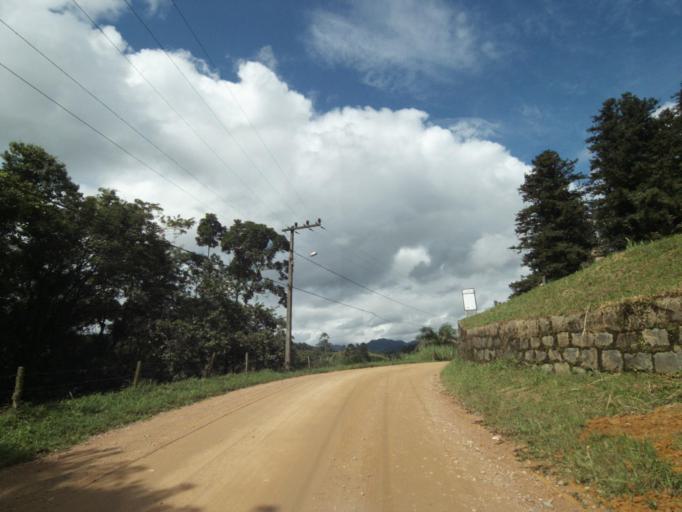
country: BR
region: Santa Catarina
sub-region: Pomerode
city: Pomerode
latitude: -26.6870
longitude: -49.1773
